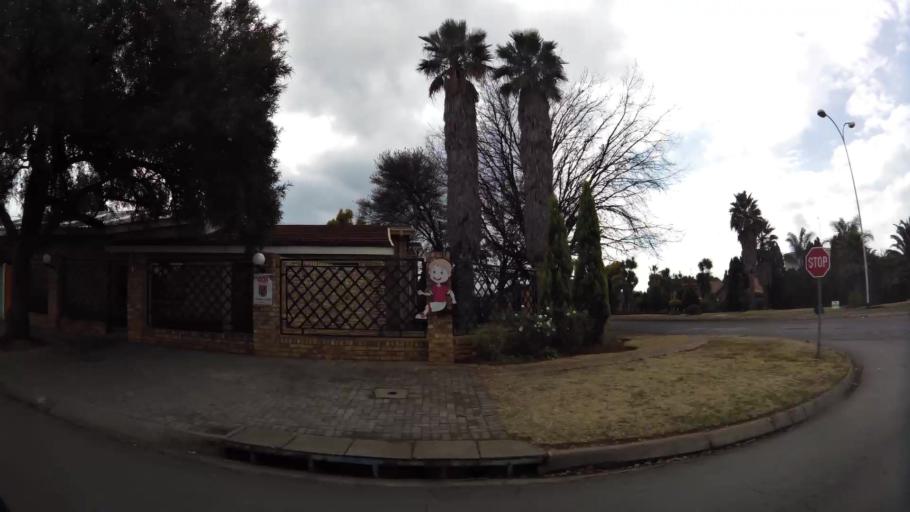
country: ZA
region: Gauteng
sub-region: Sedibeng District Municipality
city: Vanderbijlpark
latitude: -26.7365
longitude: 27.8545
